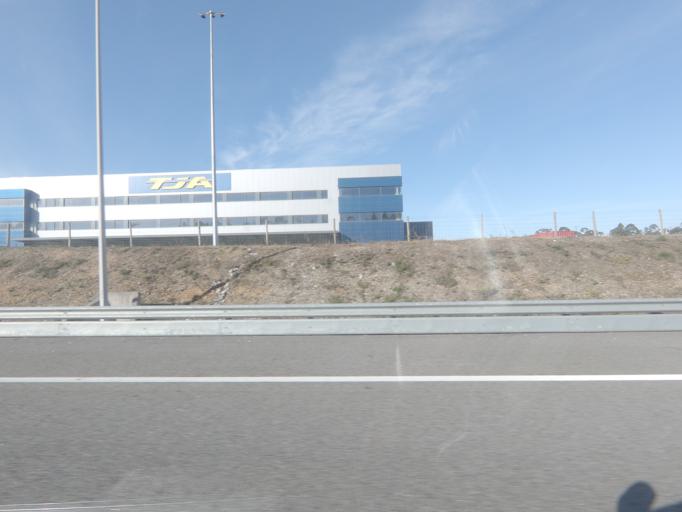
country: PT
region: Aveiro
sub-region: Estarreja
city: Beduido
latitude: 40.7844
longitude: -8.5459
